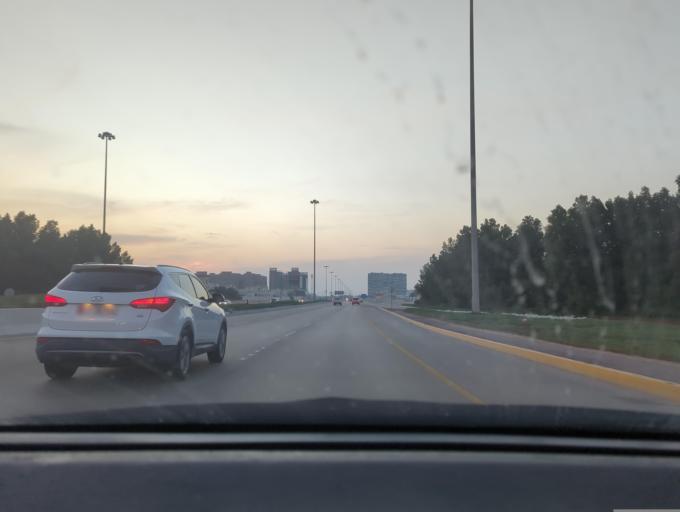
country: AE
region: Abu Dhabi
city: Abu Dhabi
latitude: 24.3750
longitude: 54.5491
